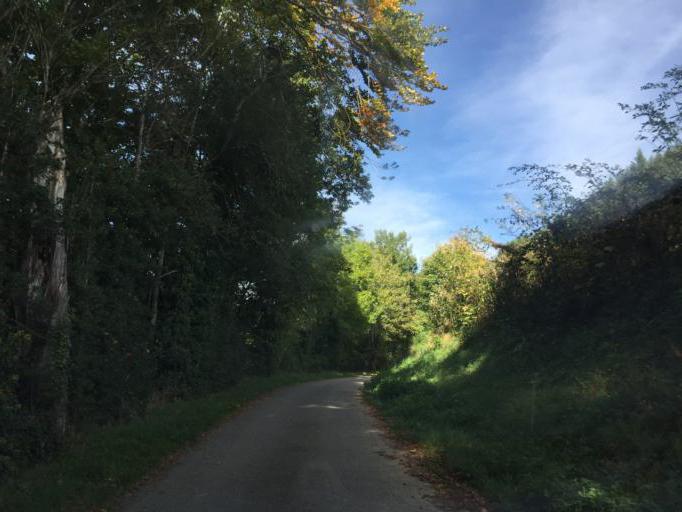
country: FR
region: Rhone-Alpes
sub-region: Departement de la Loire
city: Belmont-de-la-Loire
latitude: 46.1949
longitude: 4.4191
